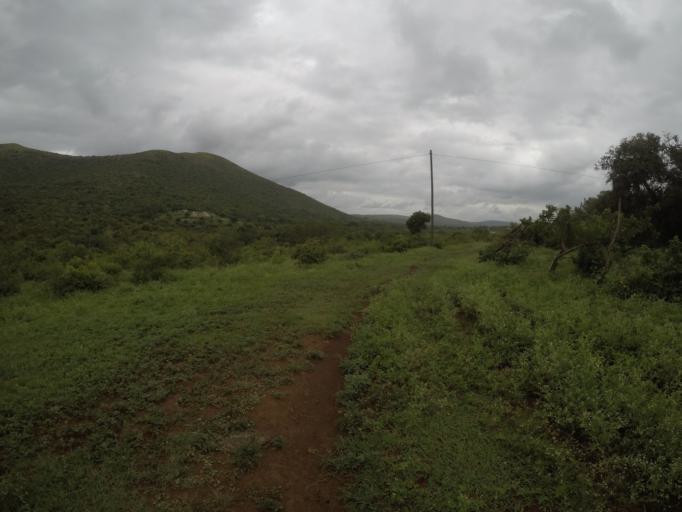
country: ZA
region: KwaZulu-Natal
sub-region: uThungulu District Municipality
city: Empangeni
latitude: -28.5869
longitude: 31.8668
